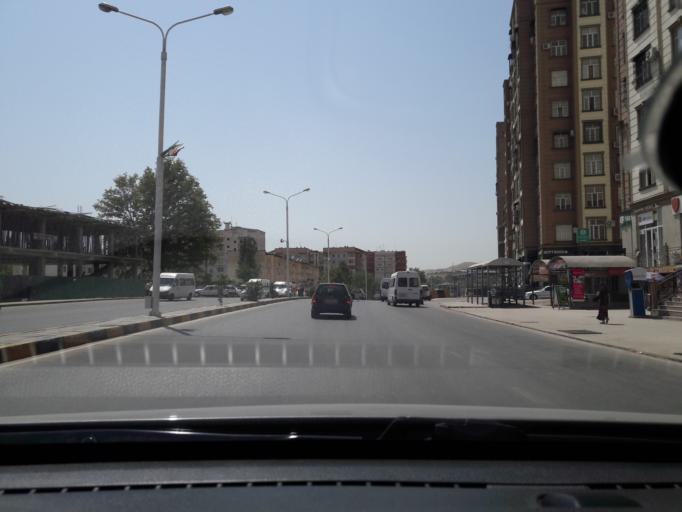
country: TJ
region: Dushanbe
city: Dushanbe
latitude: 38.5883
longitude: 68.7220
